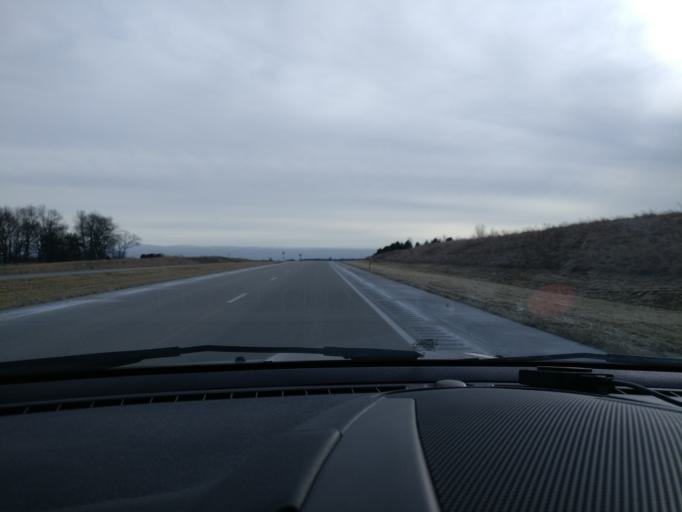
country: US
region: Nebraska
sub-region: Saunders County
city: Wahoo
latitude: 41.1786
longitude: -96.6327
